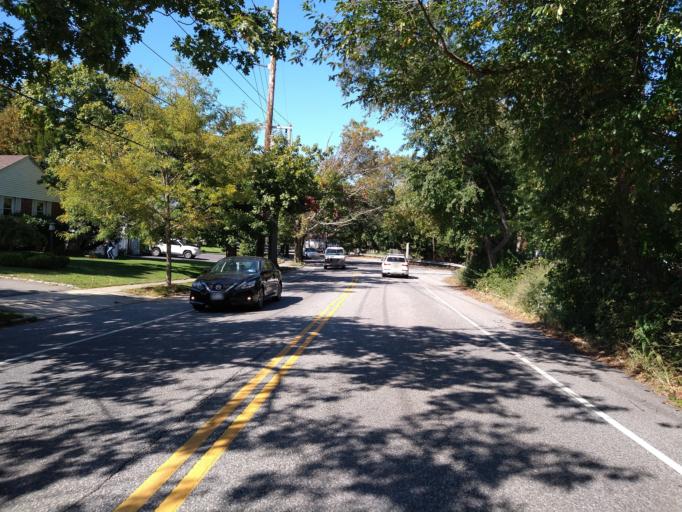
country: US
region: New York
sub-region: Nassau County
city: Syosset
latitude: 40.8272
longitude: -73.4921
